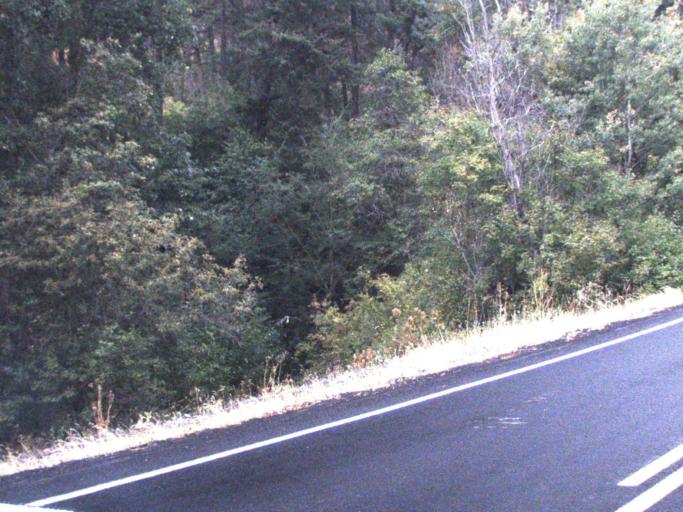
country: US
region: Washington
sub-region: Spokane County
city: Medical Lake
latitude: 47.7564
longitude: -117.8905
